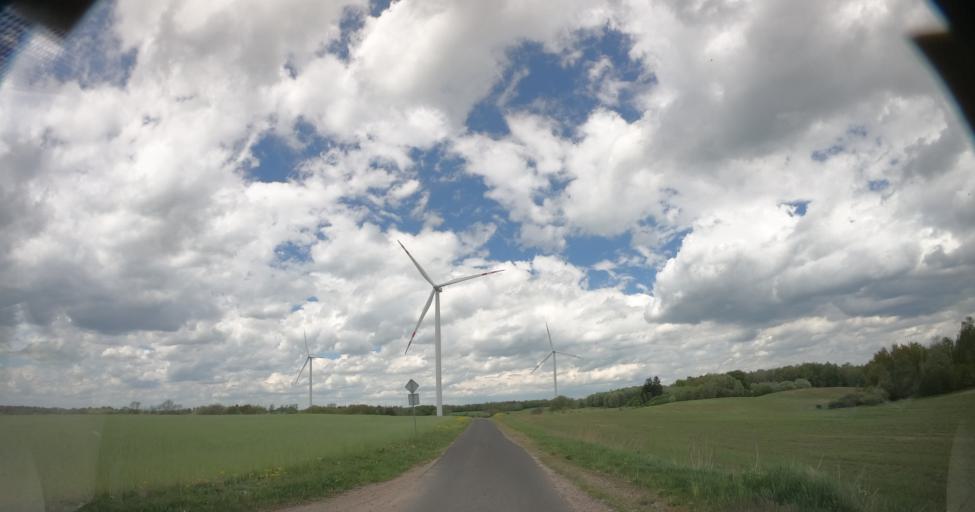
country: PL
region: West Pomeranian Voivodeship
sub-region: Powiat drawski
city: Drawsko Pomorskie
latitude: 53.5547
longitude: 15.7809
